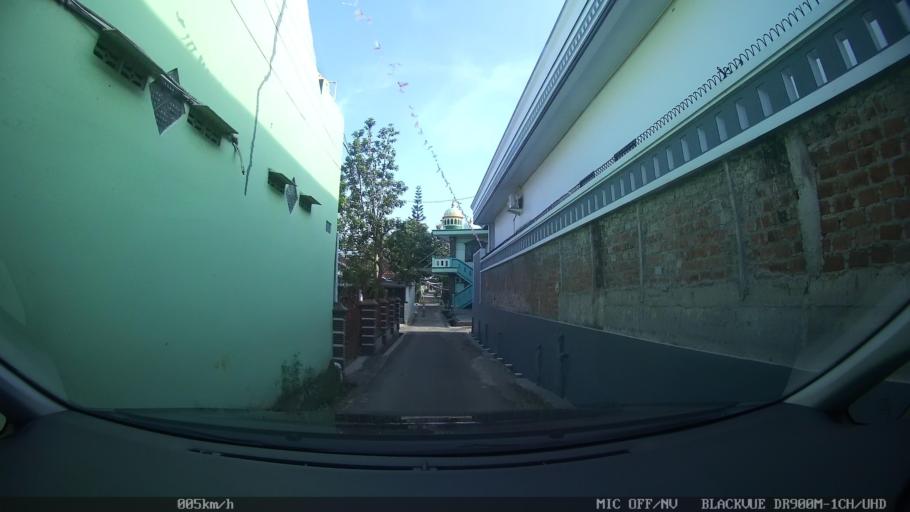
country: ID
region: Lampung
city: Kedaton
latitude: -5.3748
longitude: 105.2354
